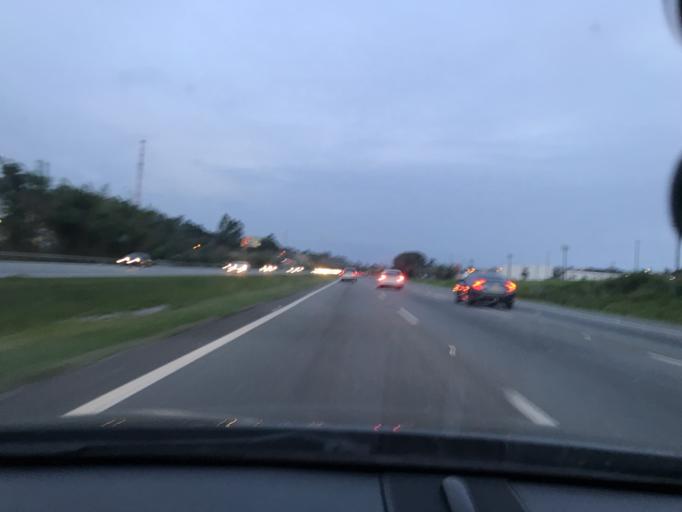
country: BR
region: Sao Paulo
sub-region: Aruja
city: Aruja
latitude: -23.4451
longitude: -46.3150
